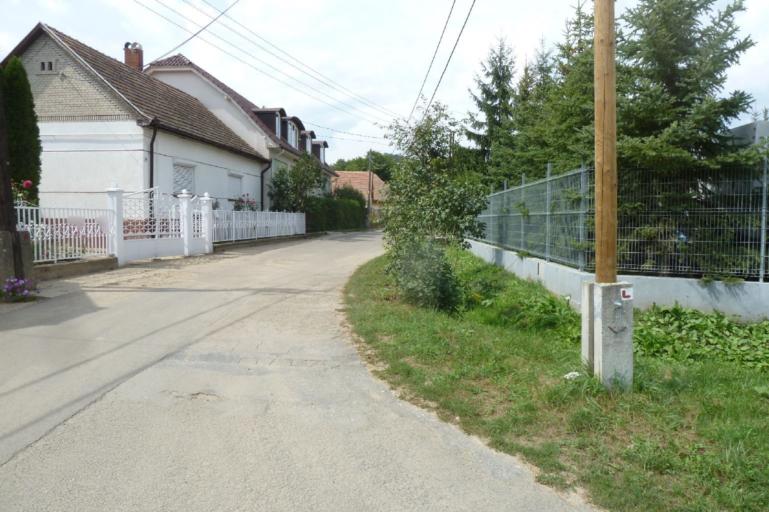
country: HU
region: Pest
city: Acsa
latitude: 47.8144
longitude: 19.3202
